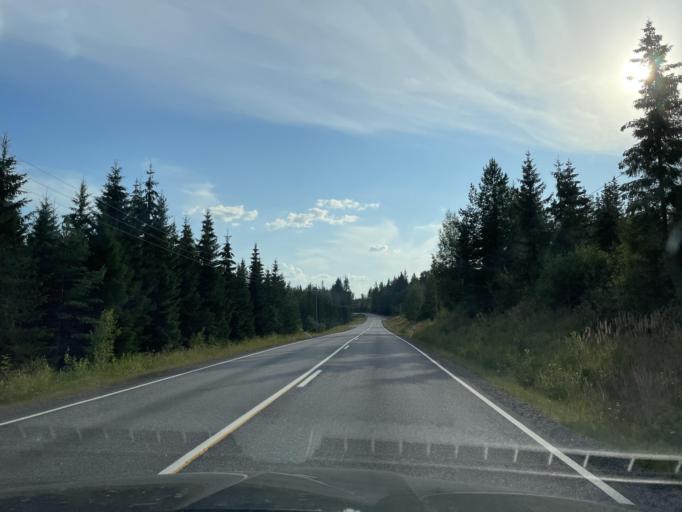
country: FI
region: Paijanne Tavastia
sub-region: Lahti
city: Auttoinen
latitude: 61.3262
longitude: 25.1735
